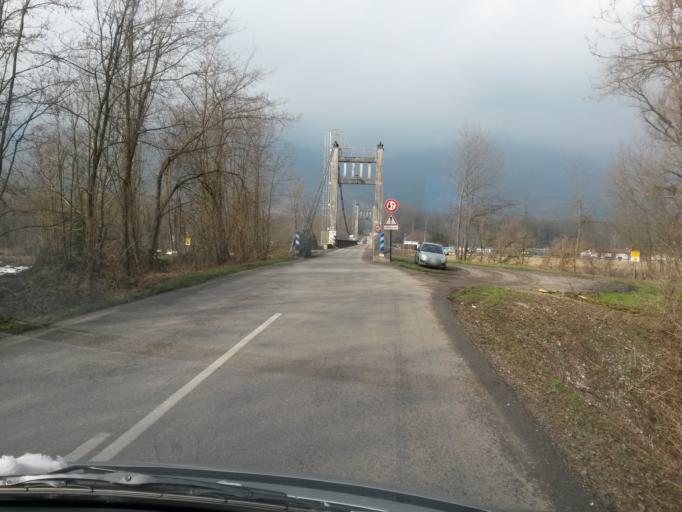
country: FR
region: Rhone-Alpes
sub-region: Departement de l'Isere
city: Tencin
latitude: 45.3152
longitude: 5.9463
